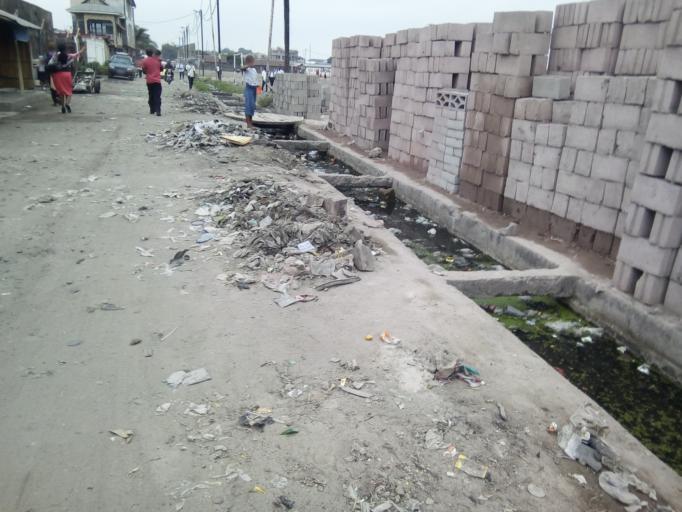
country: CD
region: Kinshasa
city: Kinshasa
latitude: -4.3201
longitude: 15.3032
